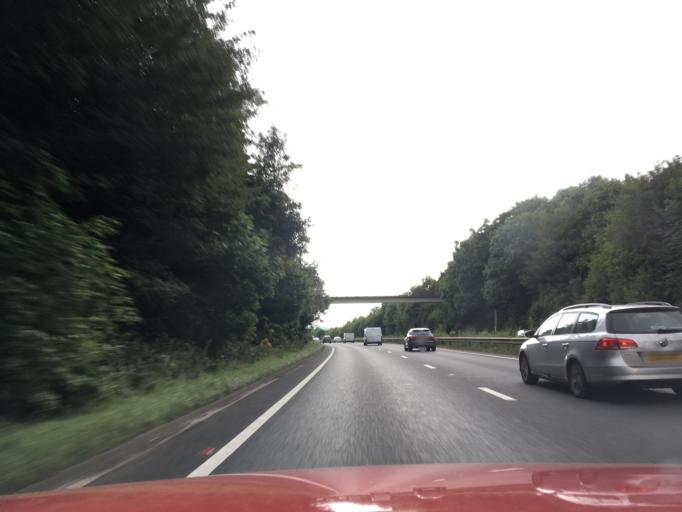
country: GB
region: England
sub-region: Hampshire
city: Petersfield
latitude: 51.0142
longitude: -0.9495
